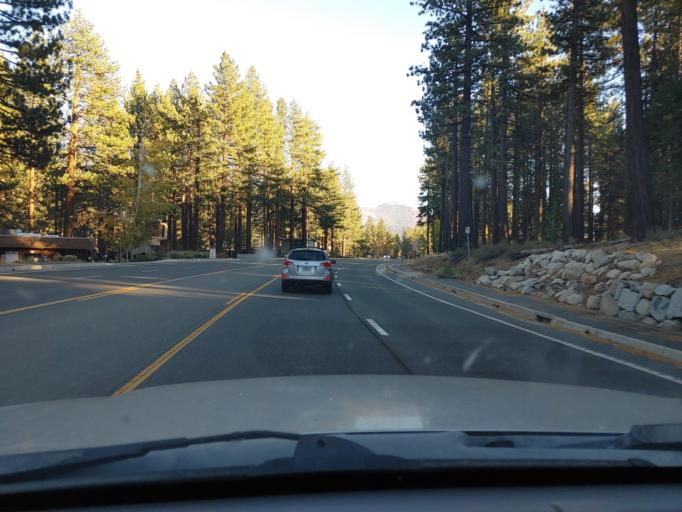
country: US
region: California
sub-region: El Dorado County
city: South Lake Tahoe
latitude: 38.9202
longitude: -120.0144
